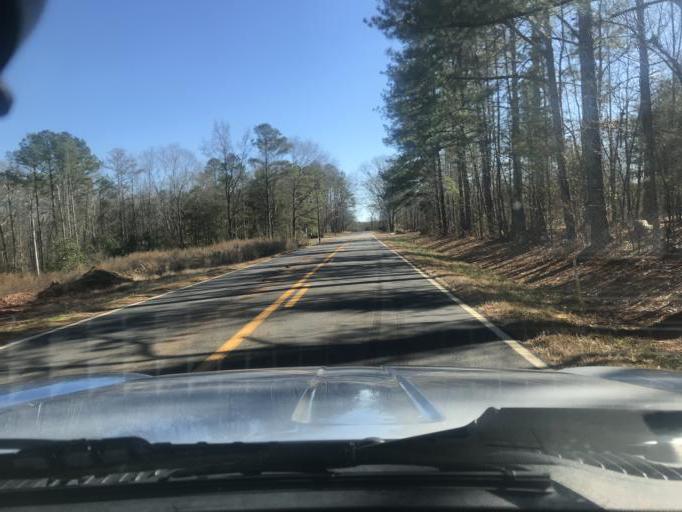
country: US
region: Georgia
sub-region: Barrow County
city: Russell
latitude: 33.9076
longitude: -83.7345
